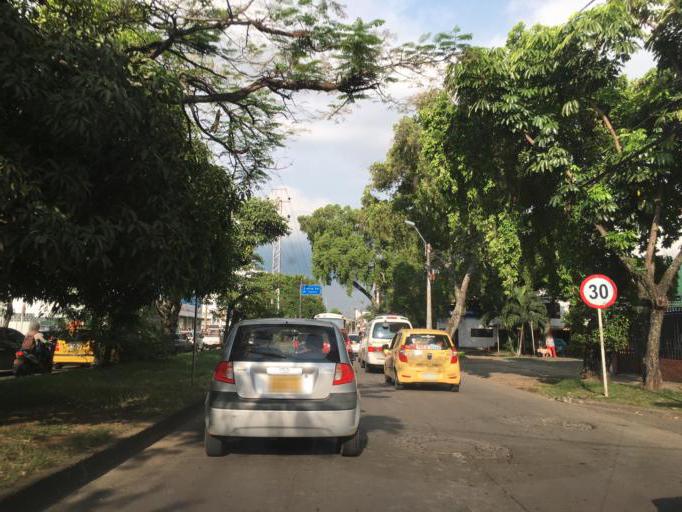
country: CO
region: Valle del Cauca
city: Cali
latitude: 3.4170
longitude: -76.5413
